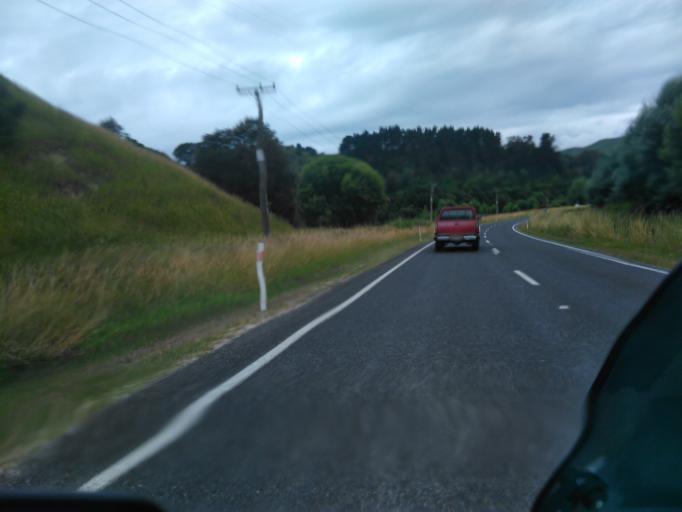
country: NZ
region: Gisborne
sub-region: Gisborne District
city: Gisborne
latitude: -38.4568
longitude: 177.7466
